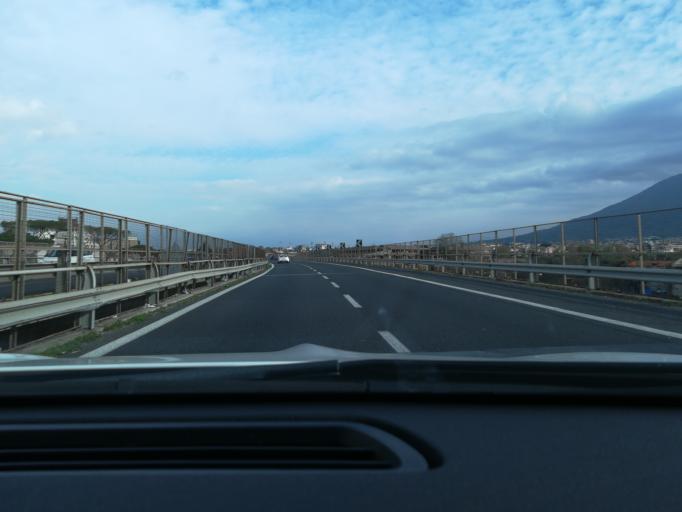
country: IT
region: Campania
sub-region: Provincia di Napoli
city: Volla
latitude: 40.8644
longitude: 14.3414
